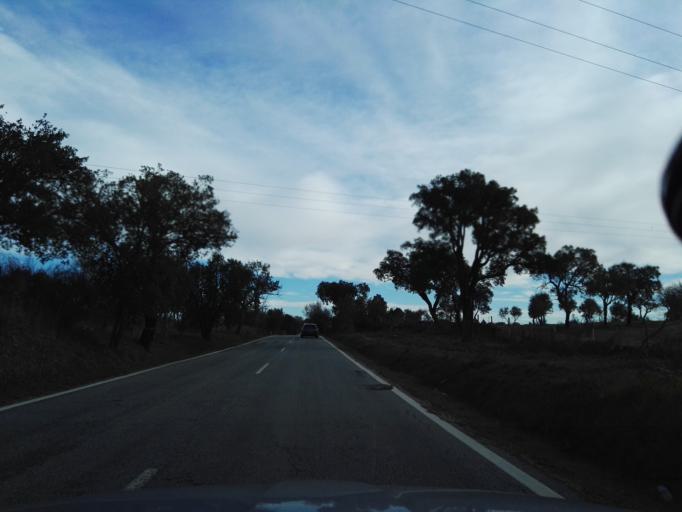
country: PT
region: Portalegre
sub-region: Nisa
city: Nisa
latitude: 39.4925
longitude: -7.7145
